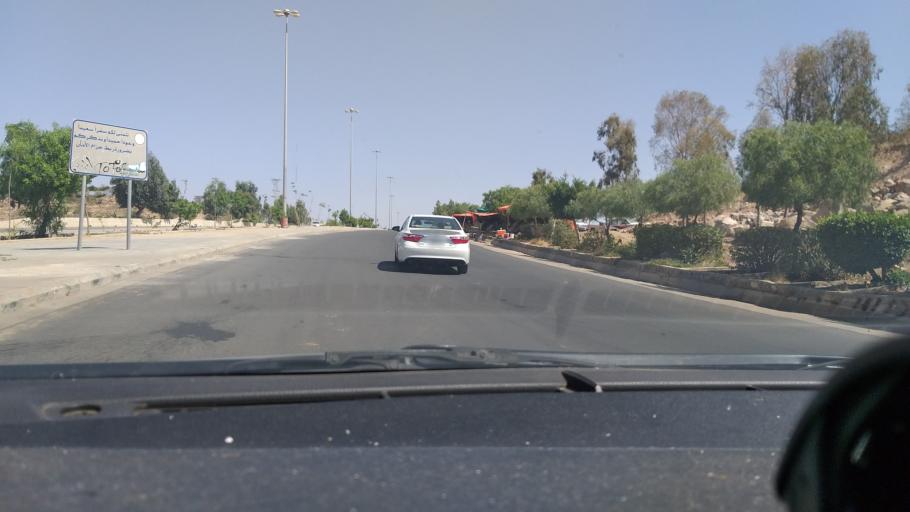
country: SA
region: Makkah
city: Ash Shafa
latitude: 21.0811
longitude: 40.3155
